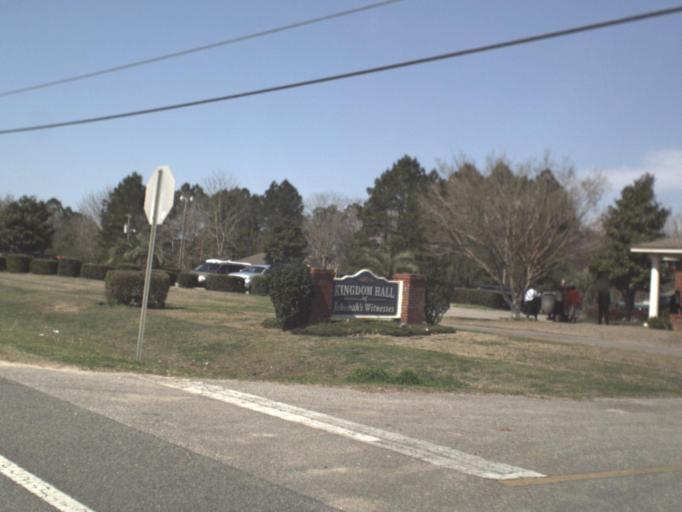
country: US
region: Florida
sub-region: Gadsden County
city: Havana
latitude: 30.6190
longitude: -84.4364
